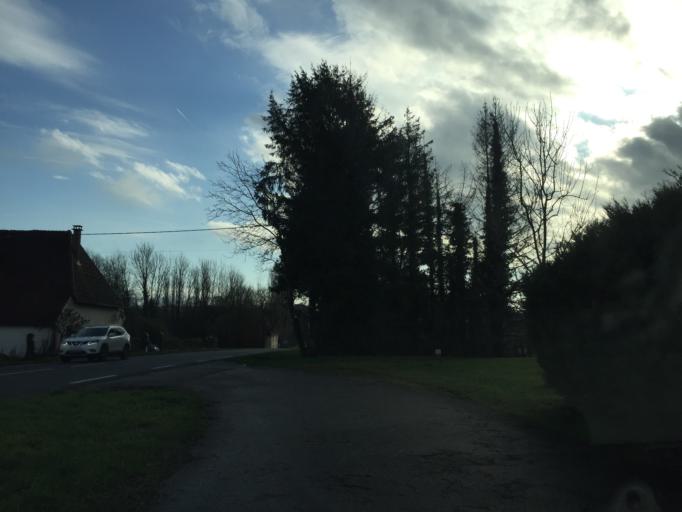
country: FR
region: Franche-Comte
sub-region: Departement du Jura
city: Mont-sous-Vaudrey
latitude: 46.9764
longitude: 5.6156
